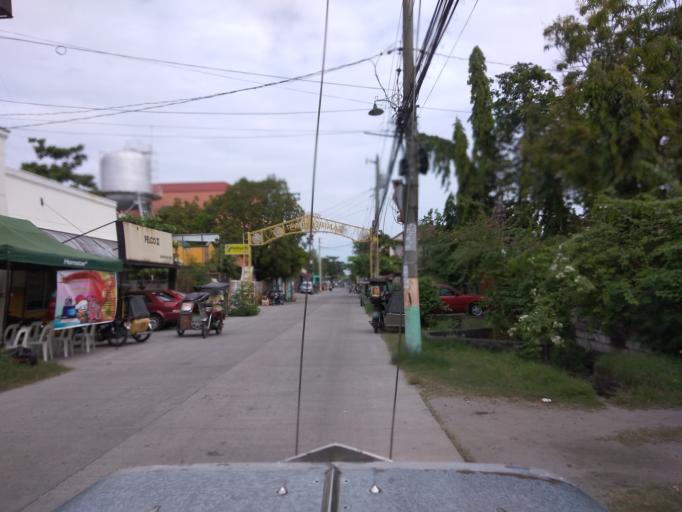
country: PH
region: Central Luzon
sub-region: Province of Pampanga
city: Sexmoan
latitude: 14.9424
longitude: 120.6218
